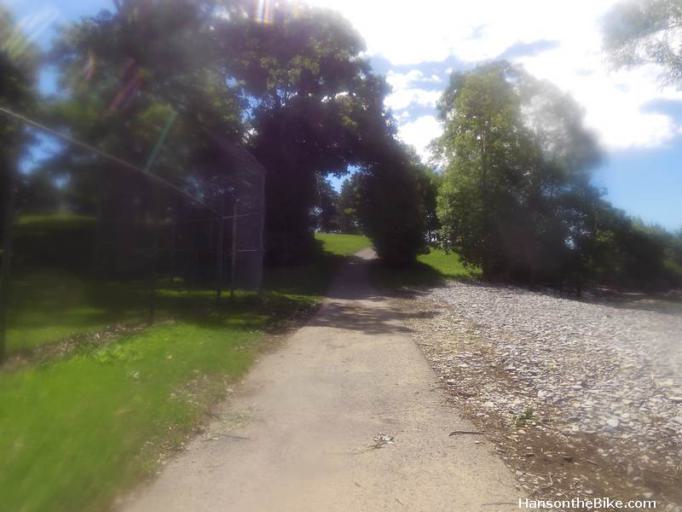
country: CA
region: Ontario
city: Kingston
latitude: 44.2145
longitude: -76.5257
